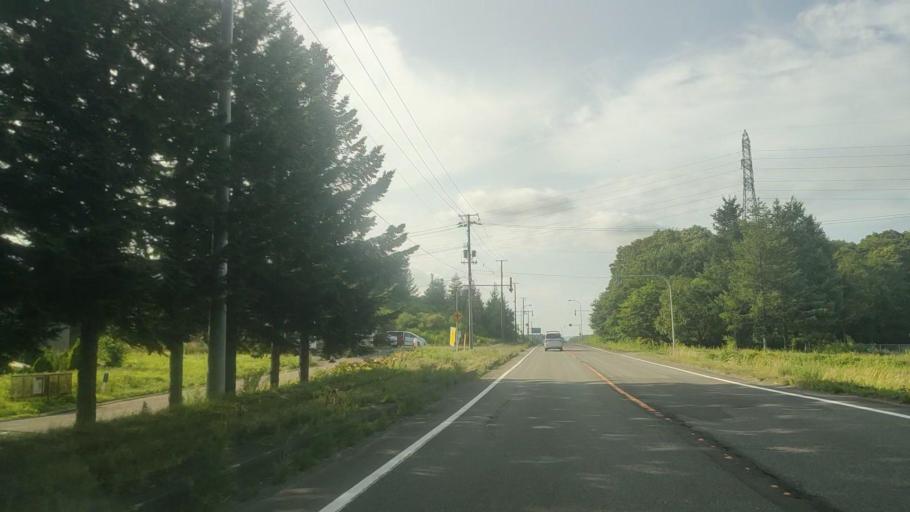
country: JP
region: Hokkaido
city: Chitose
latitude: 42.8815
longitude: 141.8144
